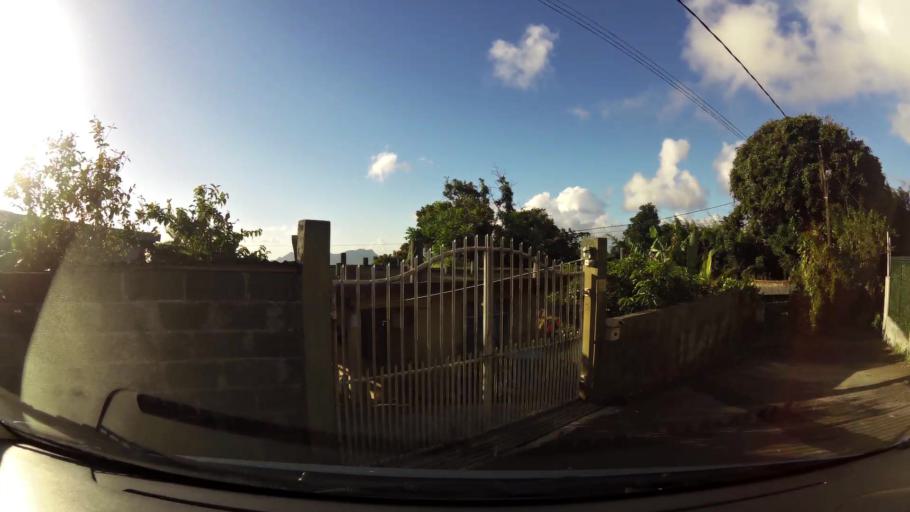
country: MU
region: Plaines Wilhems
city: Curepipe
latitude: -20.3159
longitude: 57.5133
